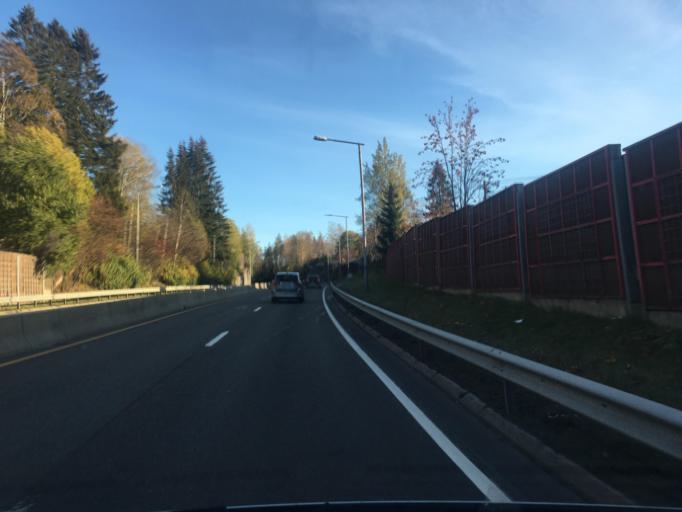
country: NO
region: Akershus
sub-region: Lorenskog
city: Kjenn
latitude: 59.9517
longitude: 10.9337
